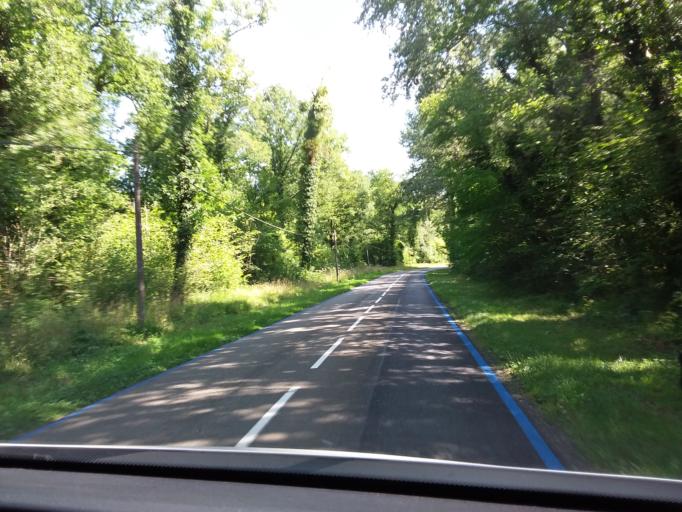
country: FR
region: Picardie
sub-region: Departement de l'Aisne
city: Saint-Erme-Outre-et-Ramecourt
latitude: 49.4507
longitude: 3.8032
